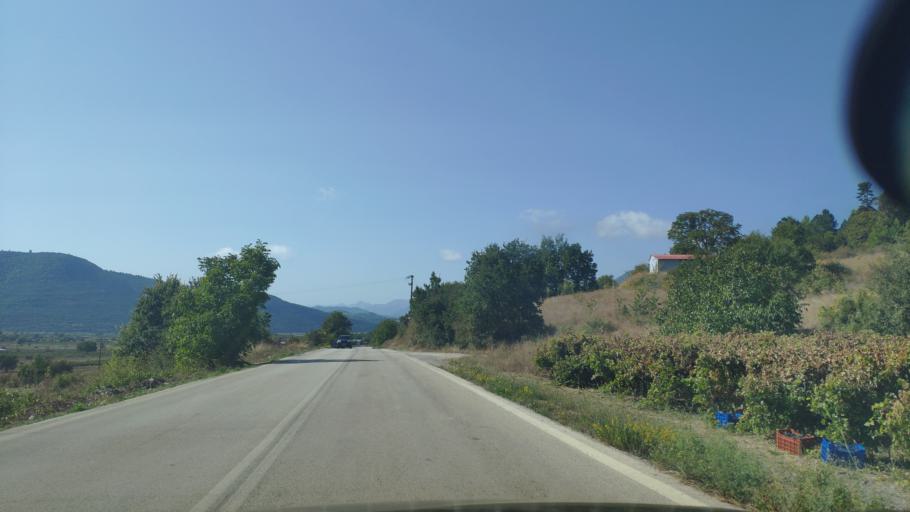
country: GR
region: Peloponnese
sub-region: Nomos Korinthias
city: Xylokastro
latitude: 37.9634
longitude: 22.5832
